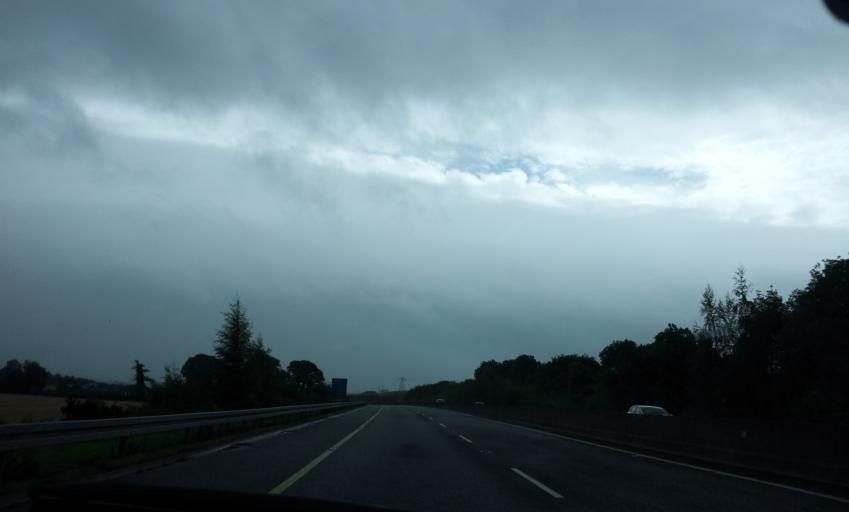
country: IE
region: Munster
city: Cahir
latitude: 52.4266
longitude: -7.9147
